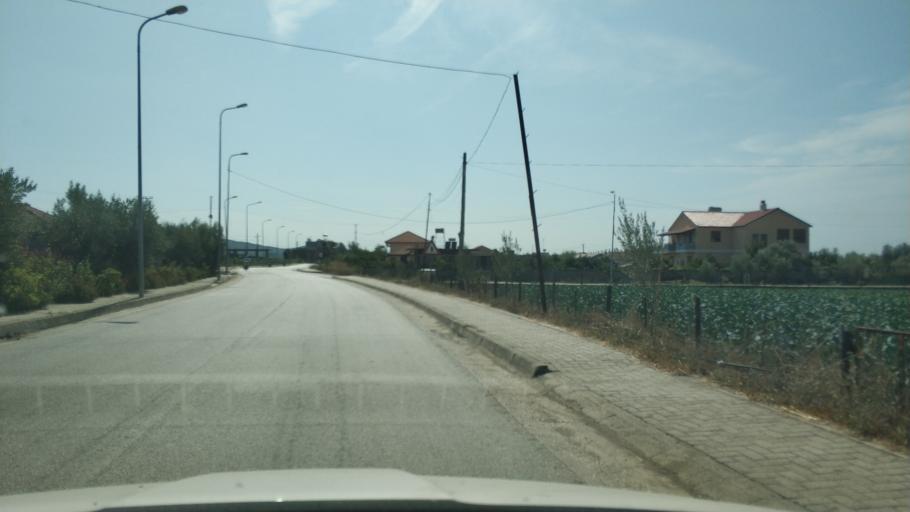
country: AL
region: Fier
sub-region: Rrethi i Lushnjes
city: Divjake
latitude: 40.9905
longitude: 19.5337
